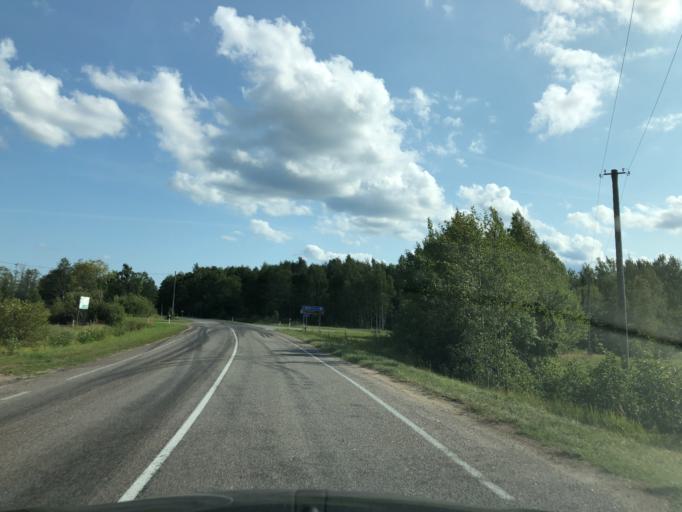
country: EE
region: Hiiumaa
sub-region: Kaerdla linn
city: Kardla
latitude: 58.7201
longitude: 22.5636
